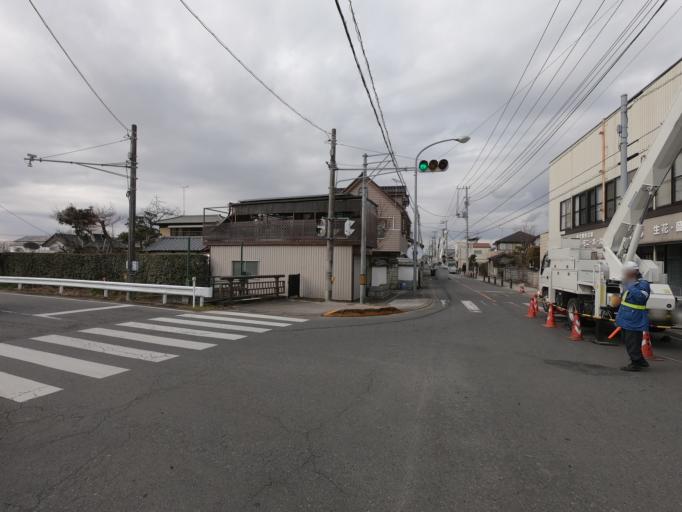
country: JP
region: Ibaraki
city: Ishioka
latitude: 36.1055
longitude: 140.4155
